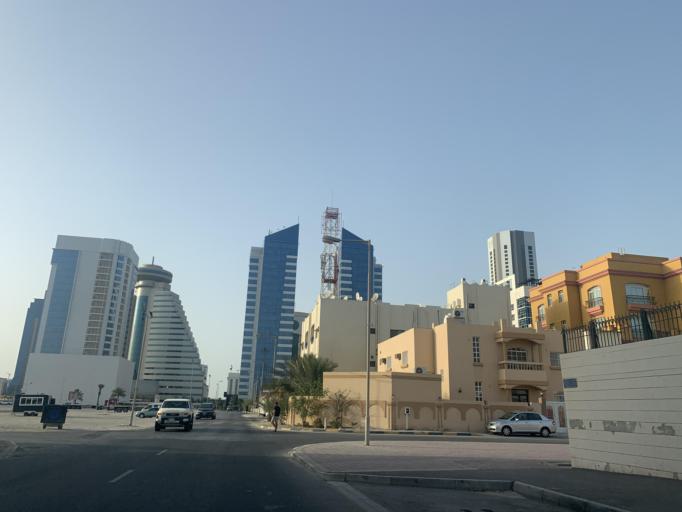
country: BH
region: Manama
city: Jidd Hafs
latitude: 26.2270
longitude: 50.5453
